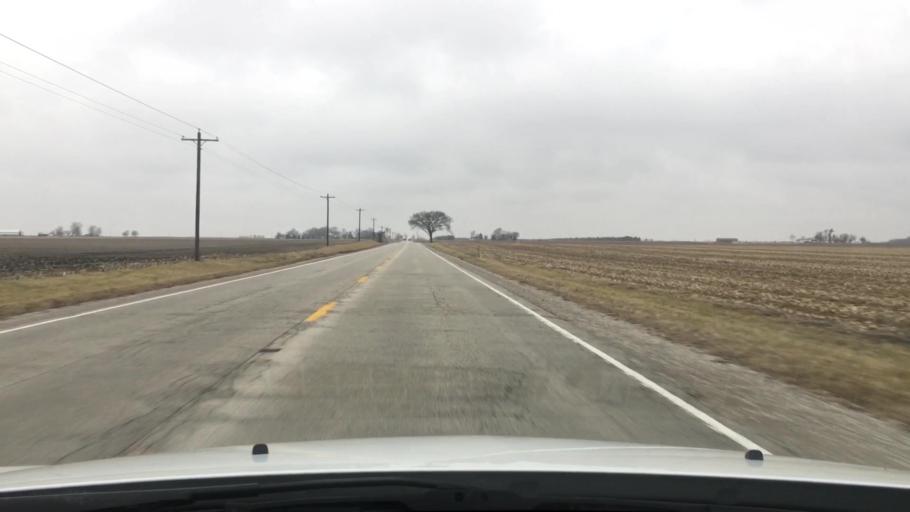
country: US
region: Illinois
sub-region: Iroquois County
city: Clifton
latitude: 40.8876
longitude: -87.8505
